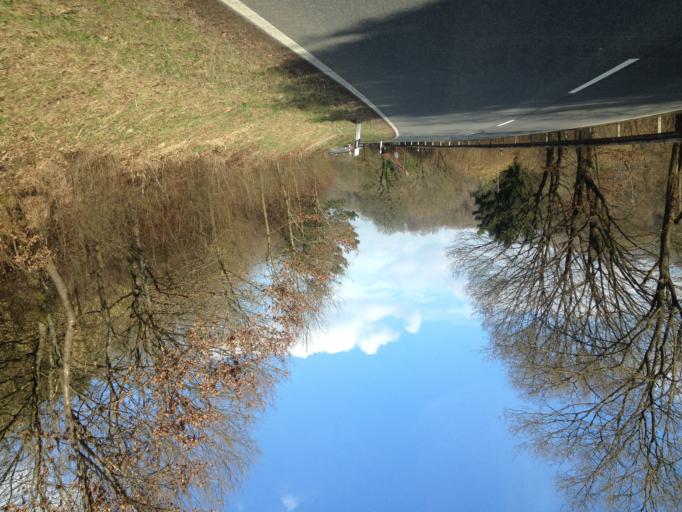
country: DE
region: Saarland
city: Sankt Wendel
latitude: 49.4428
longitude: 7.1471
